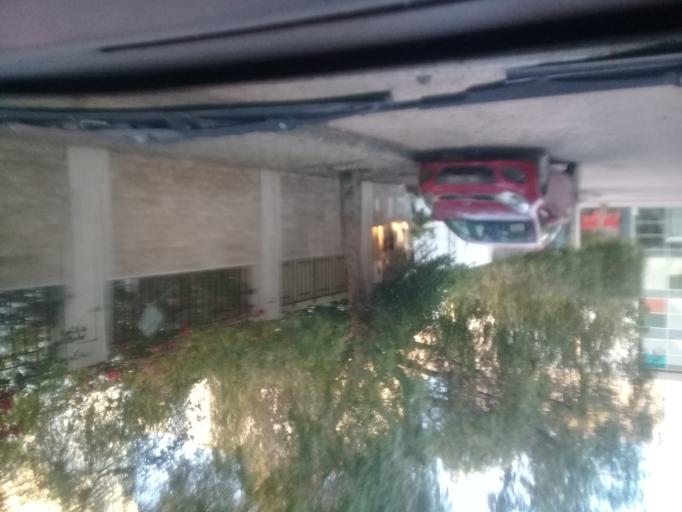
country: TN
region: Tunis
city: La Goulette
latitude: 36.8464
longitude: 10.2651
